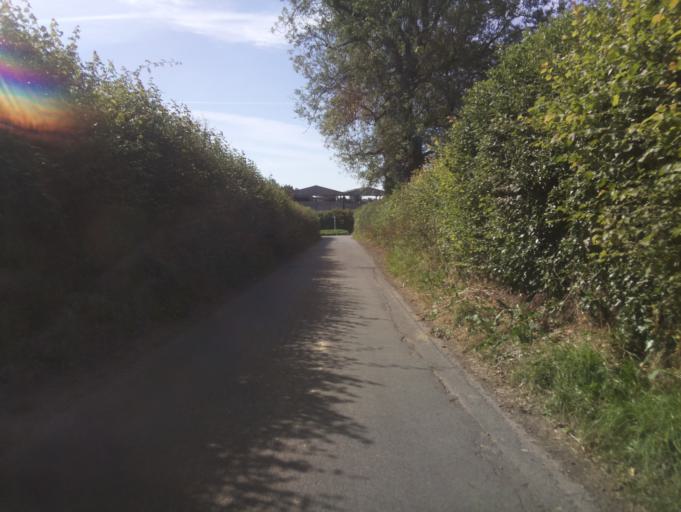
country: GB
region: England
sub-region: Wiltshire
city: Nettleton
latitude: 51.5048
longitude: -2.2598
